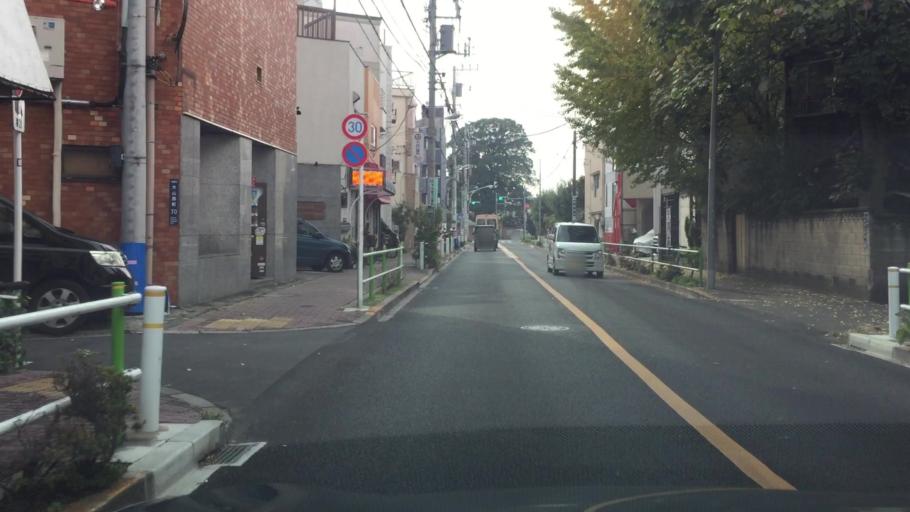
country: JP
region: Tokyo
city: Tokyo
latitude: 35.7478
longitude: 139.6937
